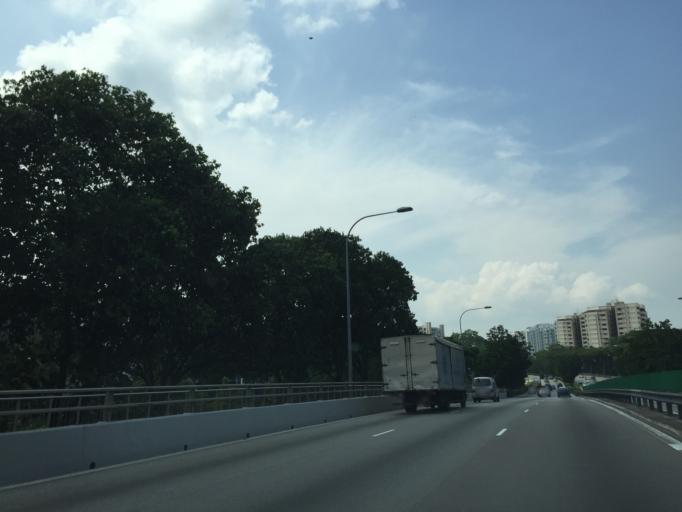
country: SG
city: Singapore
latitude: 1.3263
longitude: 103.9061
